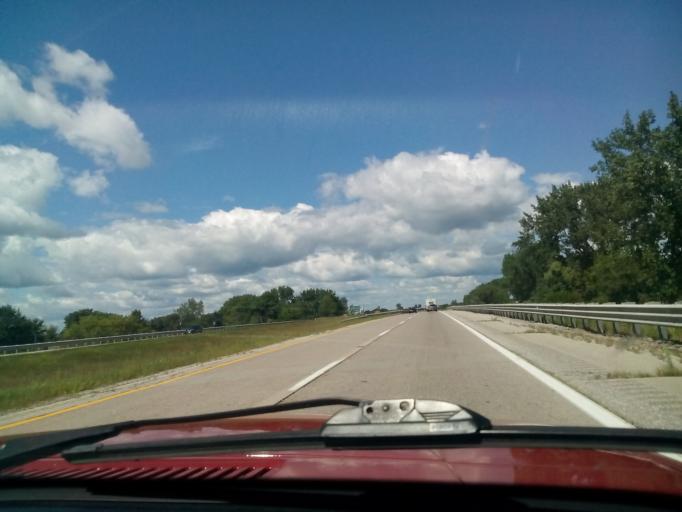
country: US
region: Michigan
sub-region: Bay County
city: Bay City
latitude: 43.6376
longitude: -83.9714
